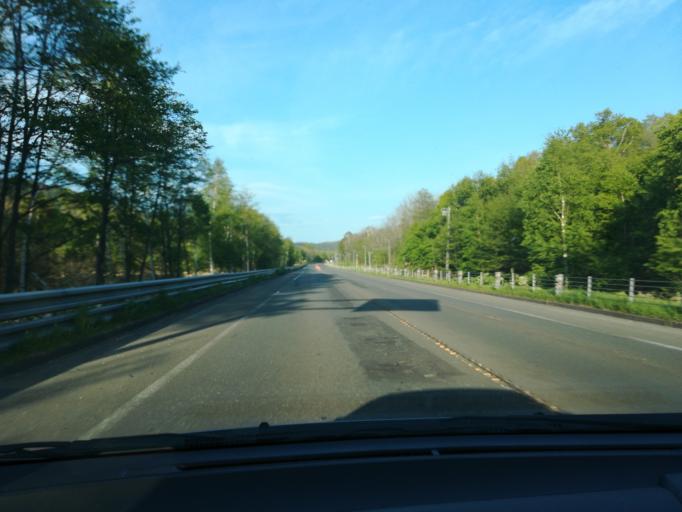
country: JP
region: Hokkaido
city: Shimo-furano
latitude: 43.1387
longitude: 142.6236
